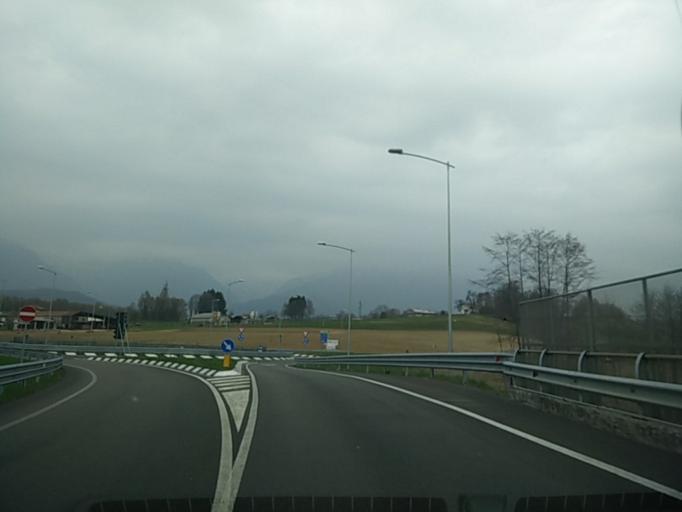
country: IT
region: Veneto
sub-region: Provincia di Belluno
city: Limana
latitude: 46.1181
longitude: 12.2071
